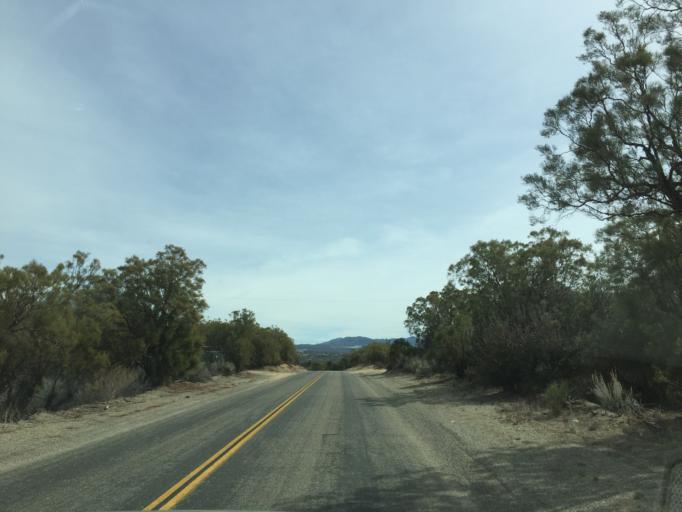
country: US
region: California
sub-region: Riverside County
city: Anza
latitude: 33.5792
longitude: -116.7471
